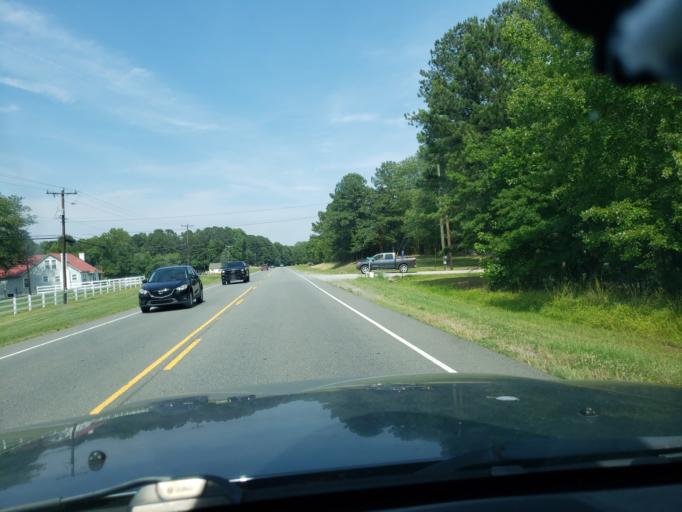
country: US
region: North Carolina
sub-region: Orange County
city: Carrboro
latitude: 35.9259
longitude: -79.1654
